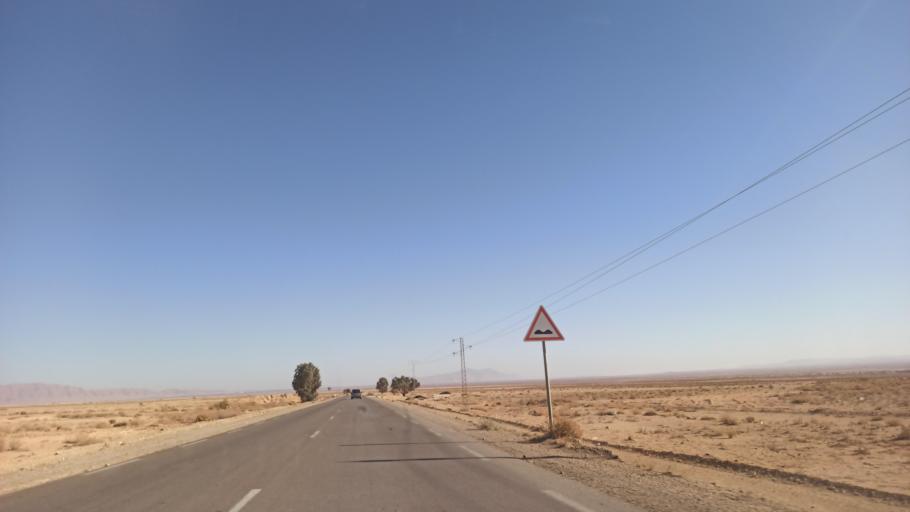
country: TN
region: Gafsa
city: Al Metlaoui
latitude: 34.3186
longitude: 8.5117
